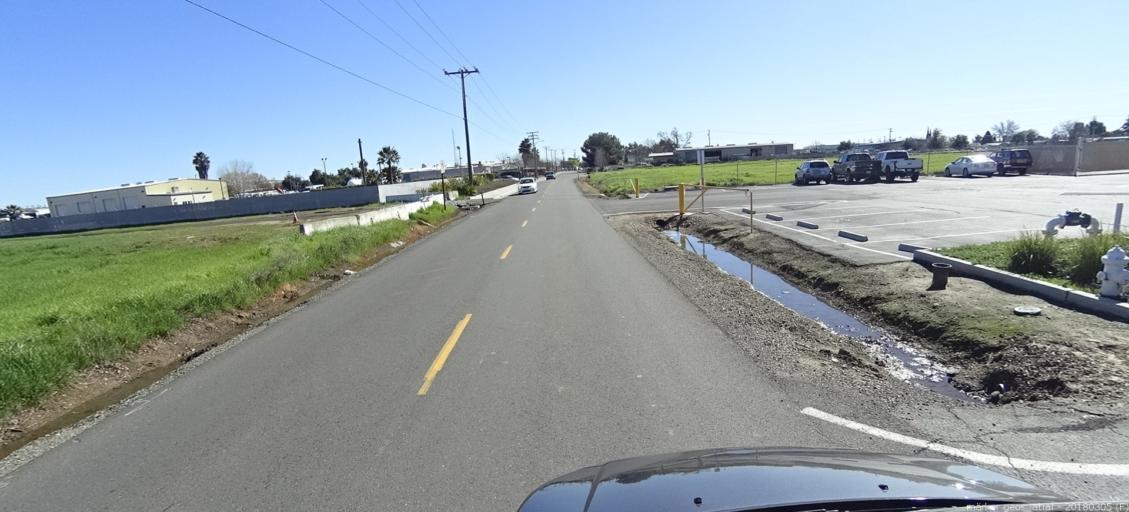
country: US
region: California
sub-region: Sacramento County
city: Florin
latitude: 38.4888
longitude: -121.3972
